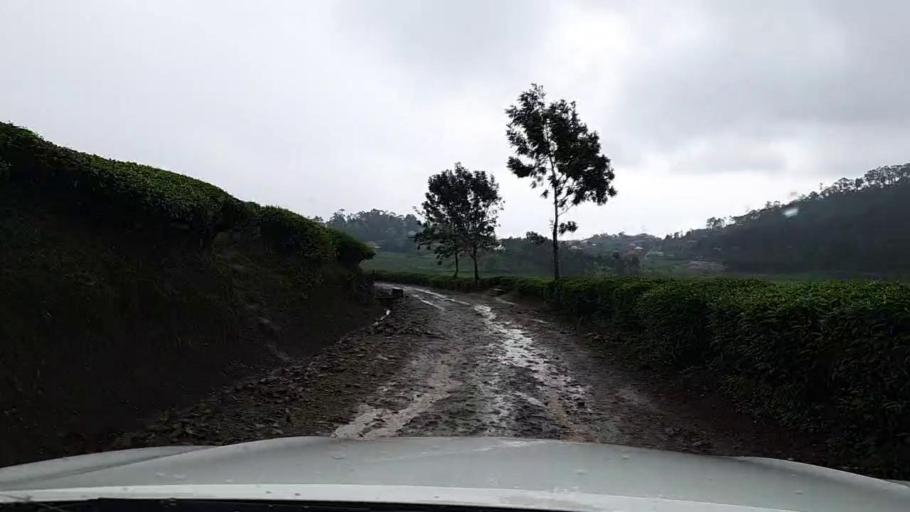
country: RW
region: Western Province
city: Cyangugu
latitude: -2.4543
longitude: 29.0396
